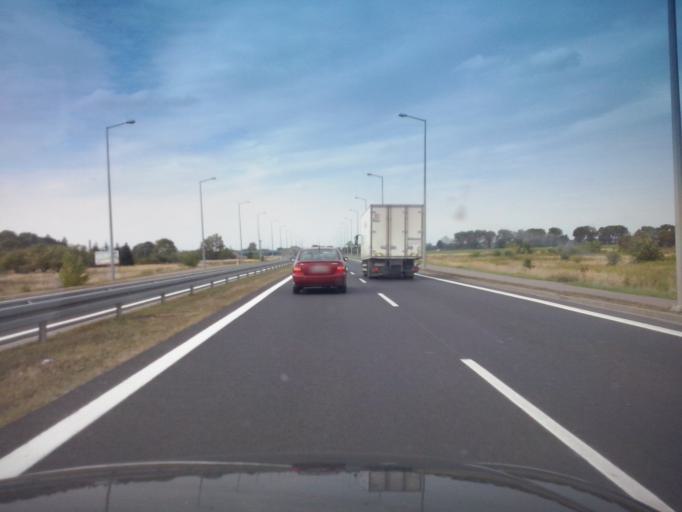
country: PL
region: Subcarpathian Voivodeship
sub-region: Powiat stalowowolski
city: Stalowa Wola
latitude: 50.6021
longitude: 22.0446
